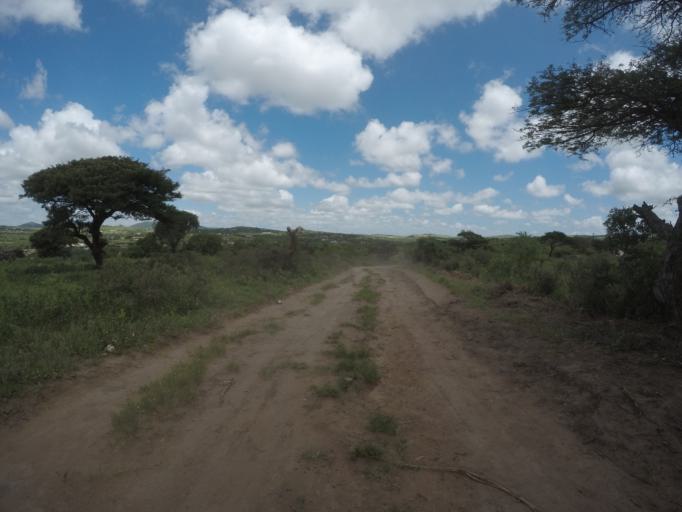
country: ZA
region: KwaZulu-Natal
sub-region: uThungulu District Municipality
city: Empangeni
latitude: -28.5867
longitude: 31.8384
